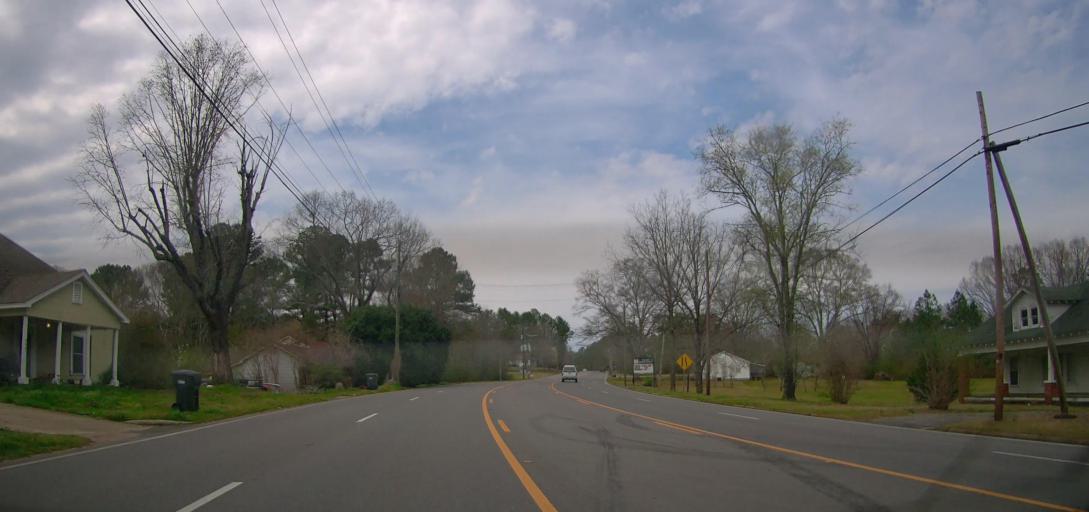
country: US
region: Alabama
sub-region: Marion County
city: Guin
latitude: 33.9783
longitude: -87.9174
